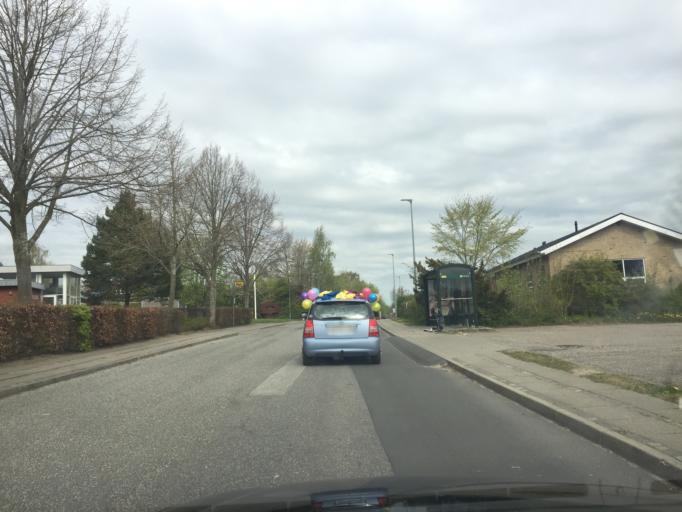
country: DK
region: South Denmark
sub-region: Kolding Kommune
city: Sonder Bjert
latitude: 55.4598
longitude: 9.5557
